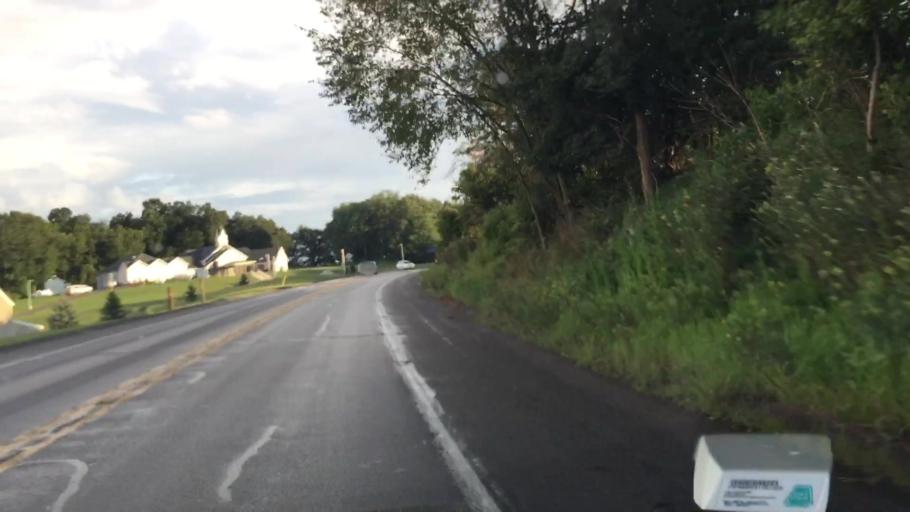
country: US
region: Pennsylvania
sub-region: Butler County
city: Meridian
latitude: 40.8181
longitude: -80.0103
